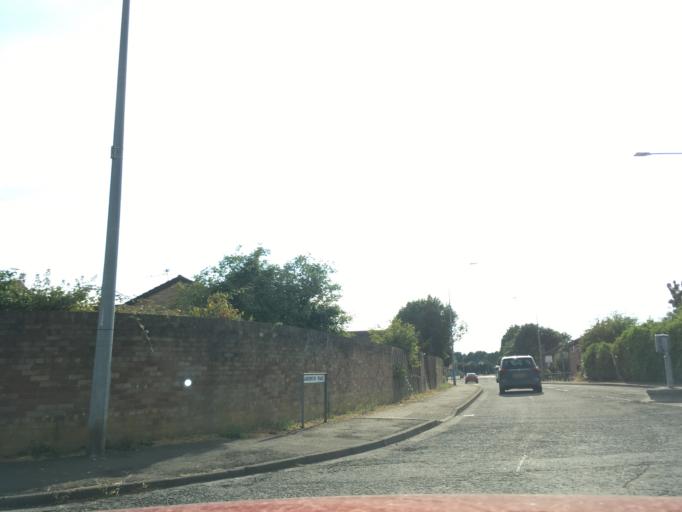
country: GB
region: Wales
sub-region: Newport
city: Marshfield
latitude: 51.5227
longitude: -3.0877
